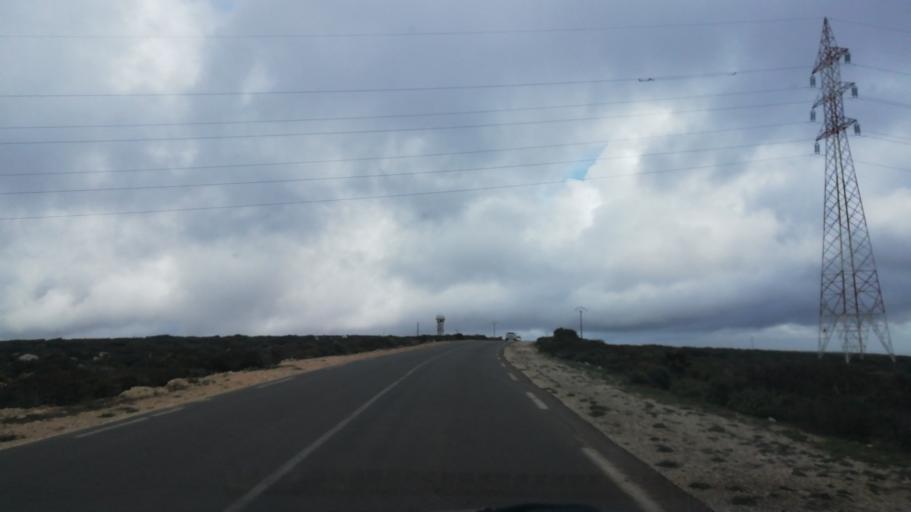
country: DZ
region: Oran
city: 'Ain el Turk
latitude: 35.6914
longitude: -0.7789
